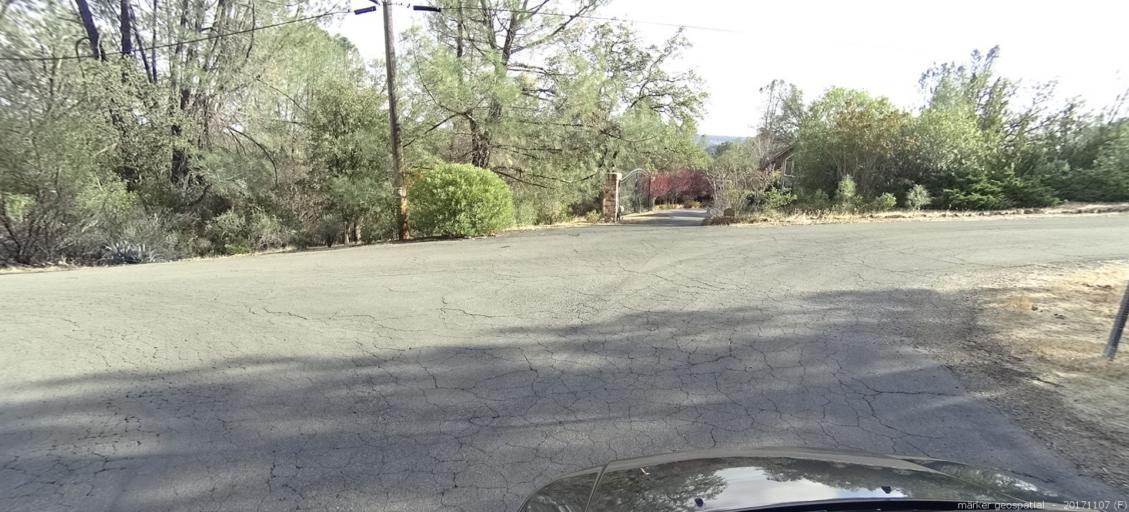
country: US
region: California
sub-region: Shasta County
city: Shasta
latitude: 40.5211
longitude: -122.5029
